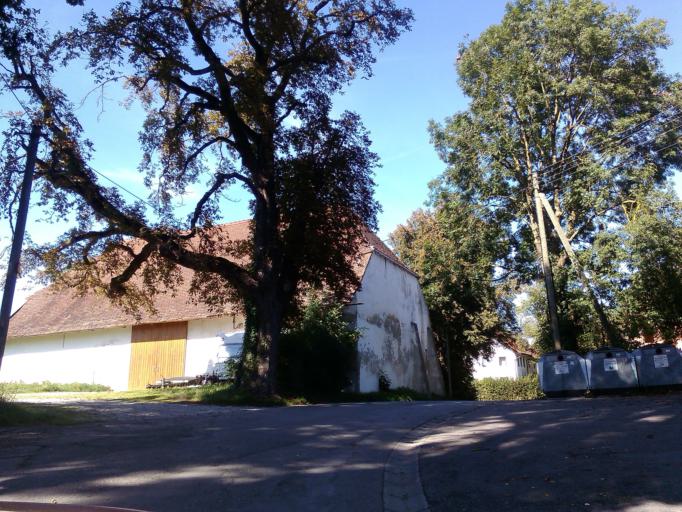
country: DE
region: Bavaria
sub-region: Upper Bavaria
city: Gilching
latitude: 48.0659
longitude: 11.3225
